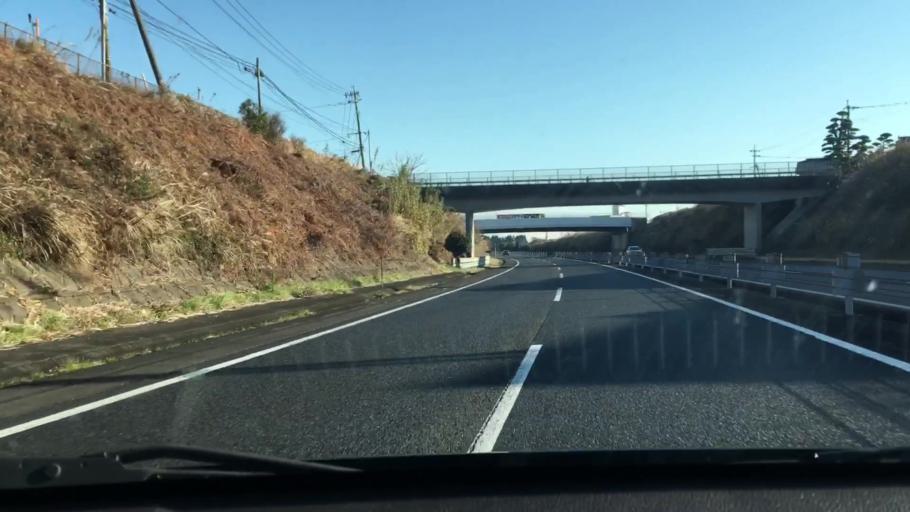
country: JP
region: Kagoshima
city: Kajiki
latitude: 31.8059
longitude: 130.7090
